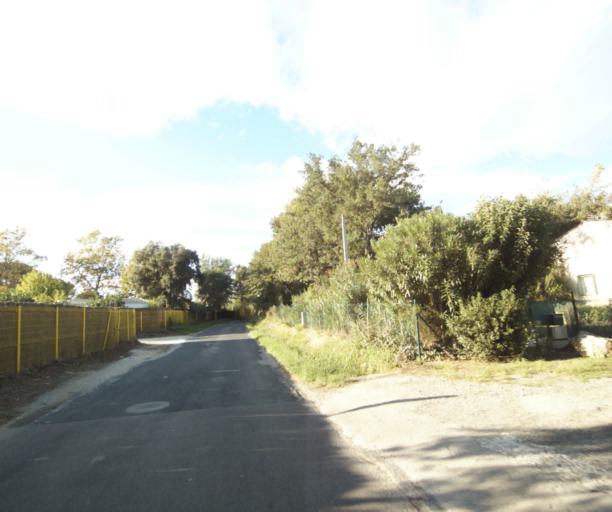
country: FR
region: Languedoc-Roussillon
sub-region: Departement des Pyrenees-Orientales
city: Argelers
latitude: 42.5588
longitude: 3.0218
